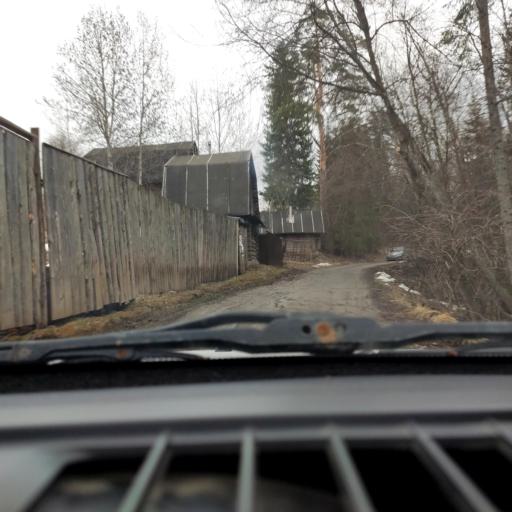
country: RU
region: Perm
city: Kultayevo
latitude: 57.8251
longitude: 55.7863
